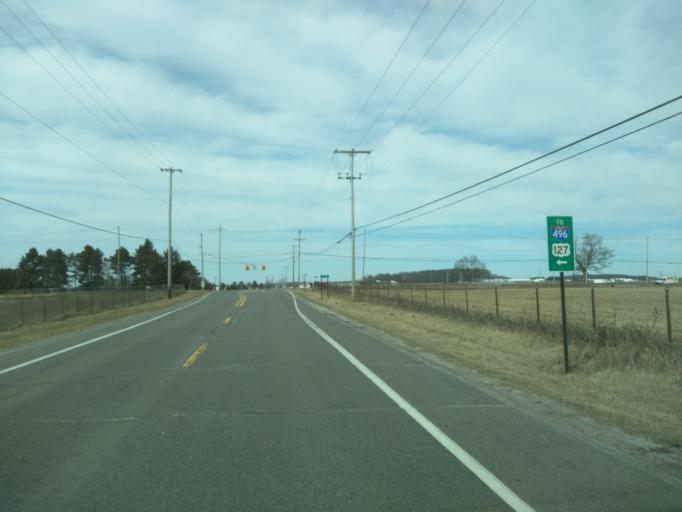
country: US
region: Michigan
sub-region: Ingham County
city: Holt
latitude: 42.6816
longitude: -84.4841
